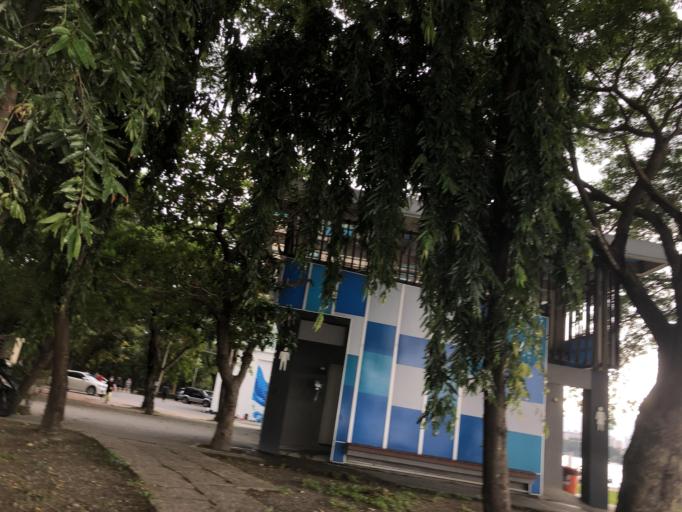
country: TW
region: Kaohsiung
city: Kaohsiung
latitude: 22.6834
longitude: 120.2984
